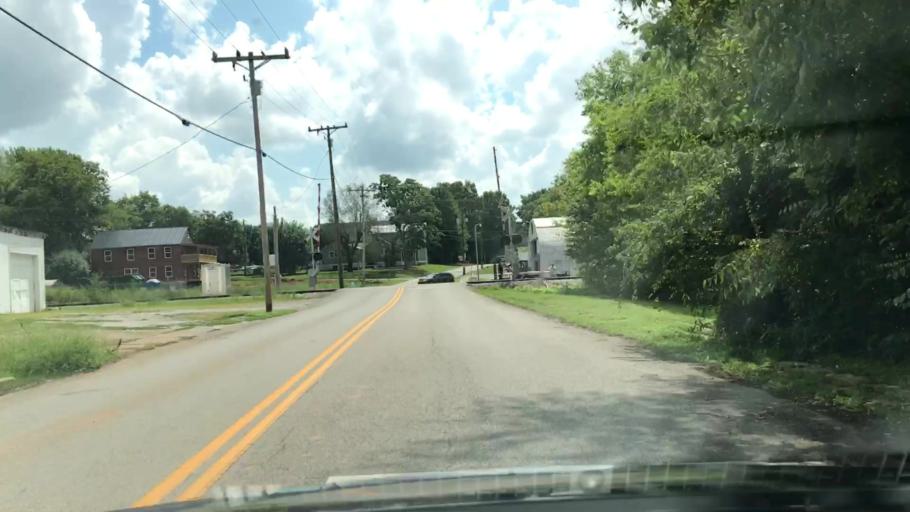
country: US
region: Kentucky
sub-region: Todd County
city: Guthrie
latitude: 36.7174
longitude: -87.0678
